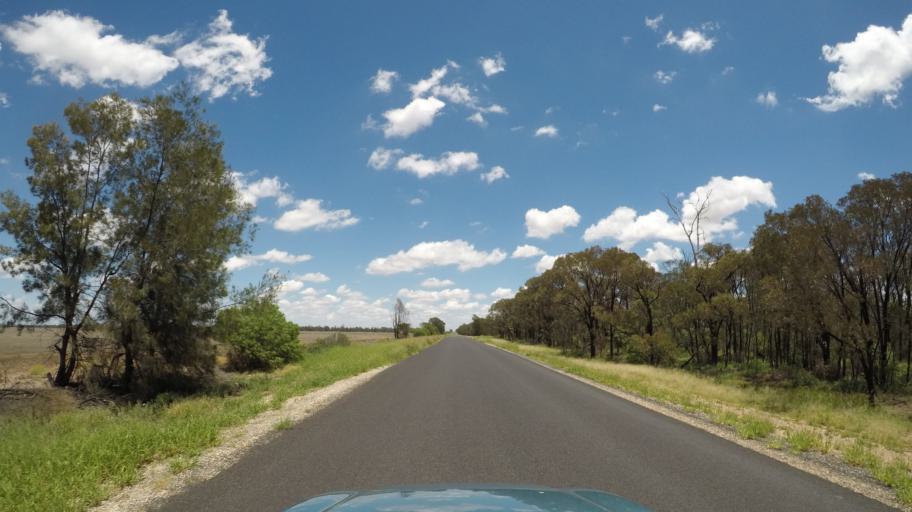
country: AU
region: Queensland
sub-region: Goondiwindi
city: Goondiwindi
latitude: -28.1632
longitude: 150.4228
